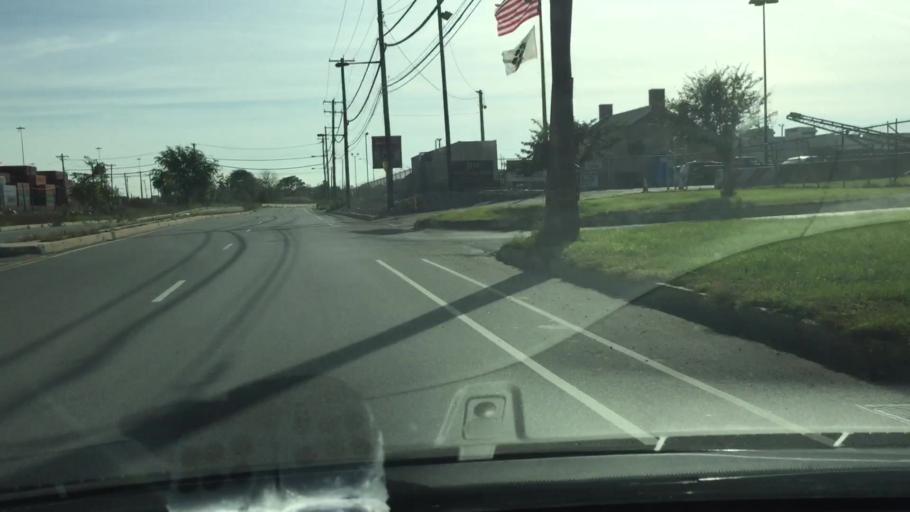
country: US
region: New Jersey
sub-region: Camden County
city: Gloucester City
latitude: 39.9064
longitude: -75.1397
